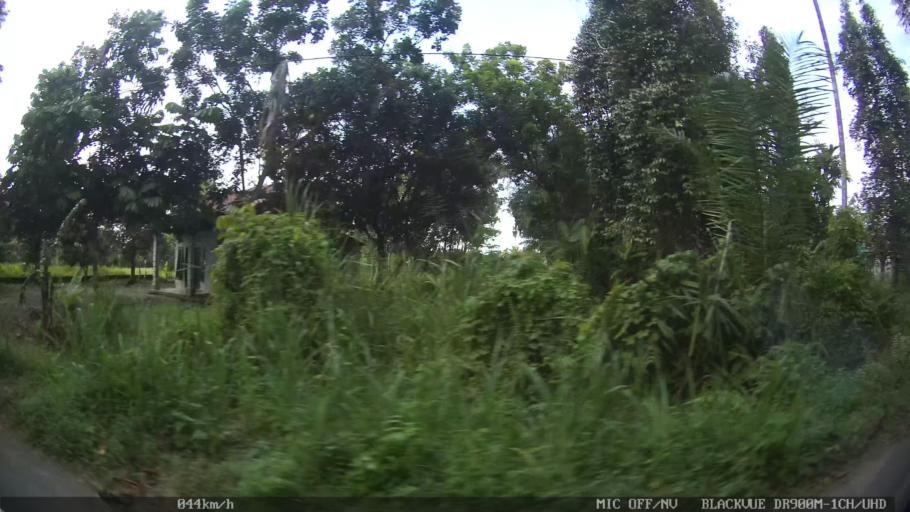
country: ID
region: North Sumatra
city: Percut
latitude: 3.5654
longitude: 98.7900
